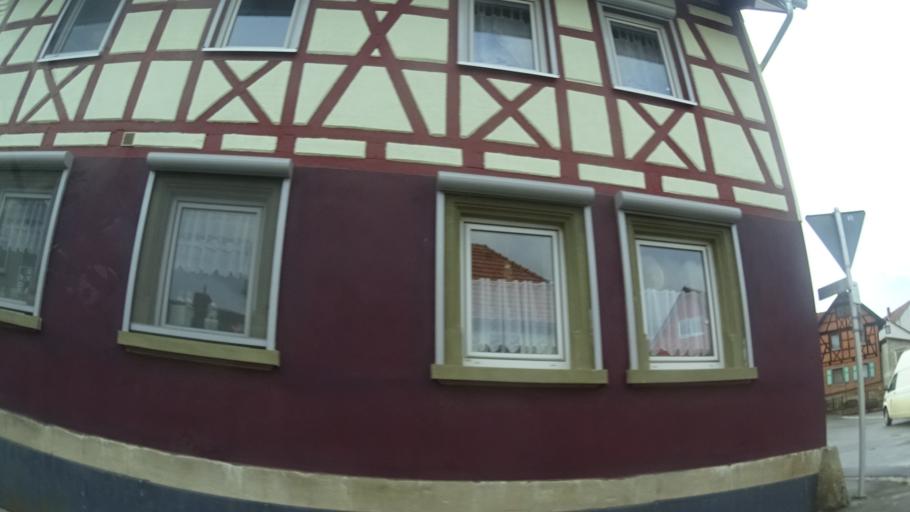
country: DE
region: Bavaria
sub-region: Regierungsbezirk Unterfranken
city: Saal an der Saale
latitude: 50.3388
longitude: 10.3860
